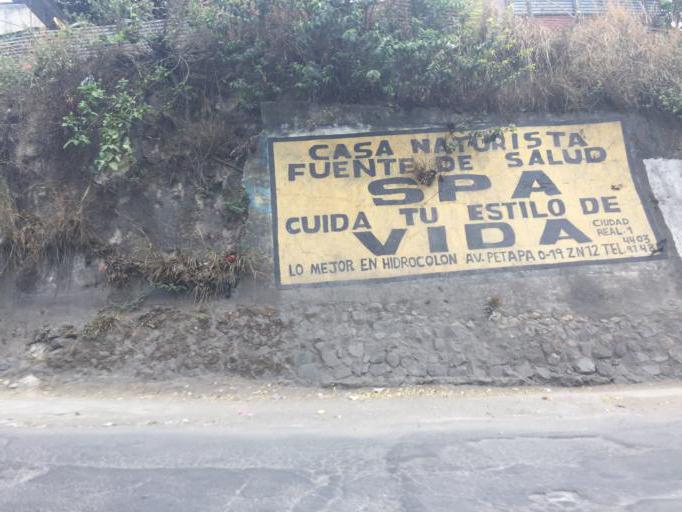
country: GT
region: Guatemala
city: Petapa
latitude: 14.5285
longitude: -90.5547
